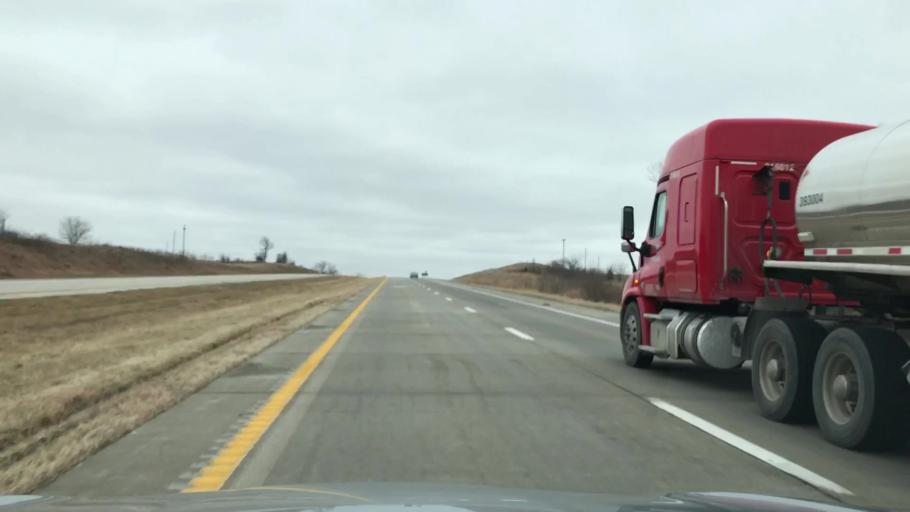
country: US
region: Missouri
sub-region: Caldwell County
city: Hamilton
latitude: 39.7353
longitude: -93.9327
